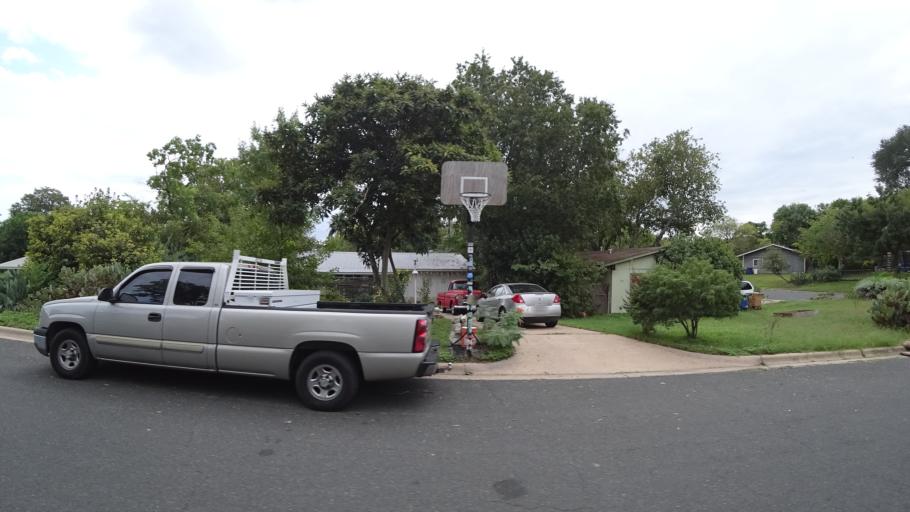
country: US
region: Texas
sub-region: Travis County
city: Rollingwood
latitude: 30.2170
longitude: -97.7783
